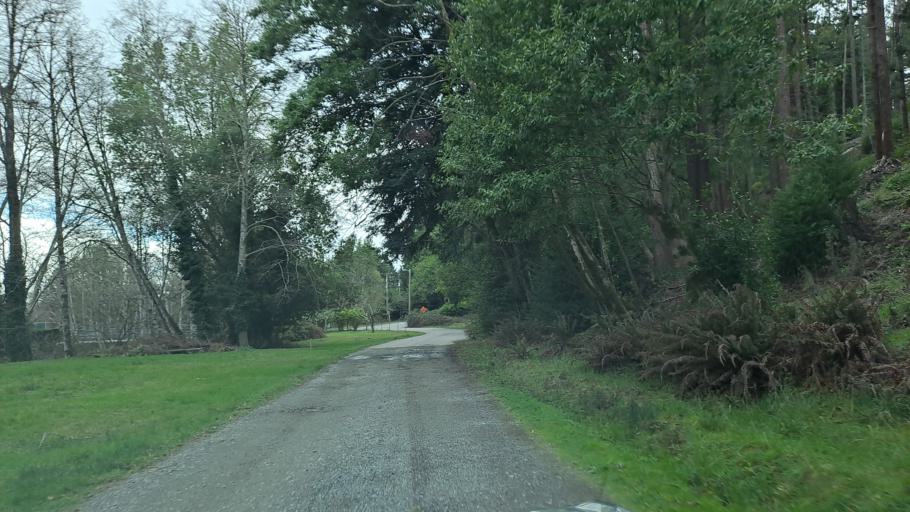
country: US
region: California
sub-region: Humboldt County
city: Fortuna
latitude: 40.6038
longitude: -124.1515
